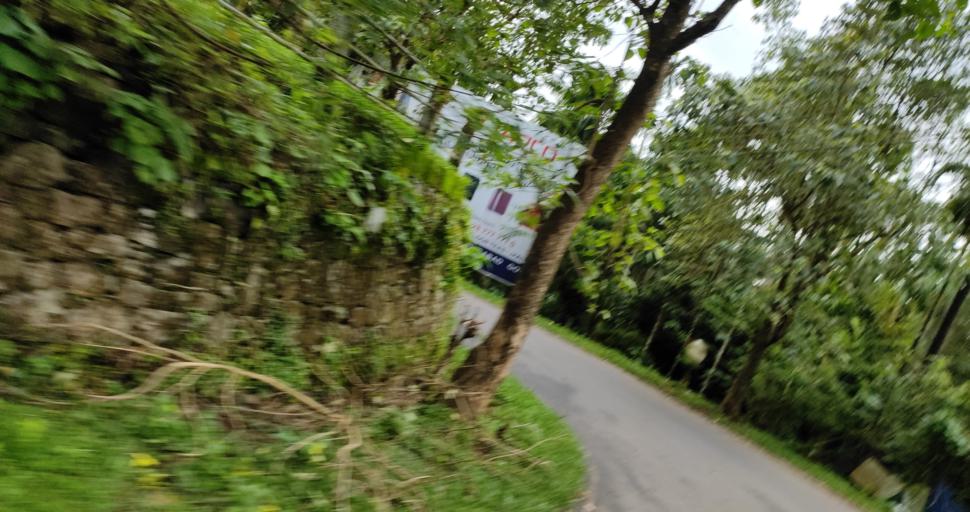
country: IN
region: Kerala
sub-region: Ernakulam
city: Angamali
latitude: 10.2896
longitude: 76.5606
